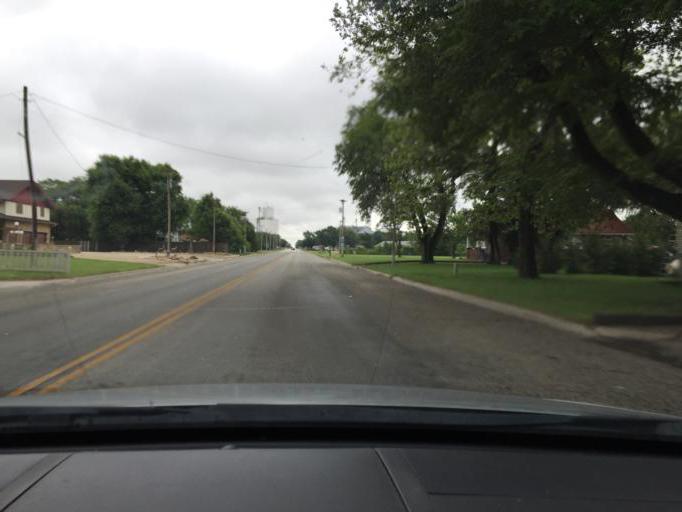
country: US
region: Kansas
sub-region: McPherson County
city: Moundridge
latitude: 38.2030
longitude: -97.5303
